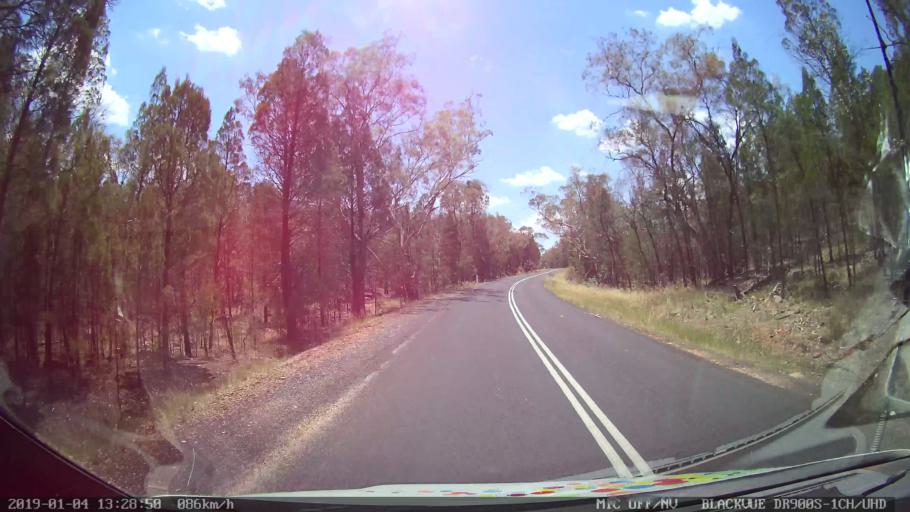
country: AU
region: New South Wales
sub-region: Parkes
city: Peak Hill
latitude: -32.6539
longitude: 148.5495
